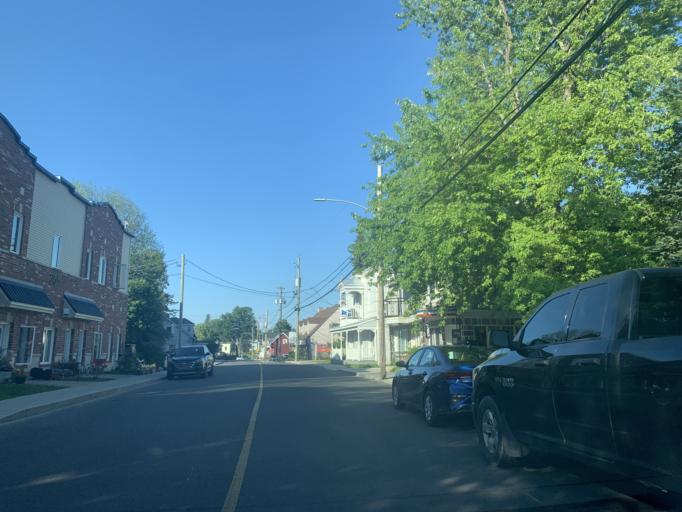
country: CA
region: Ontario
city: Hawkesbury
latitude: 45.6284
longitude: -74.6033
